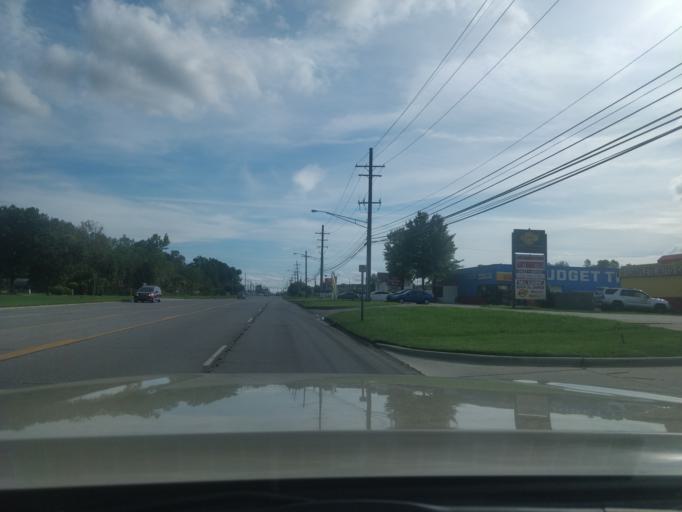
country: US
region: Michigan
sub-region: Wayne County
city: Woodhaven
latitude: 42.1589
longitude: -83.2268
